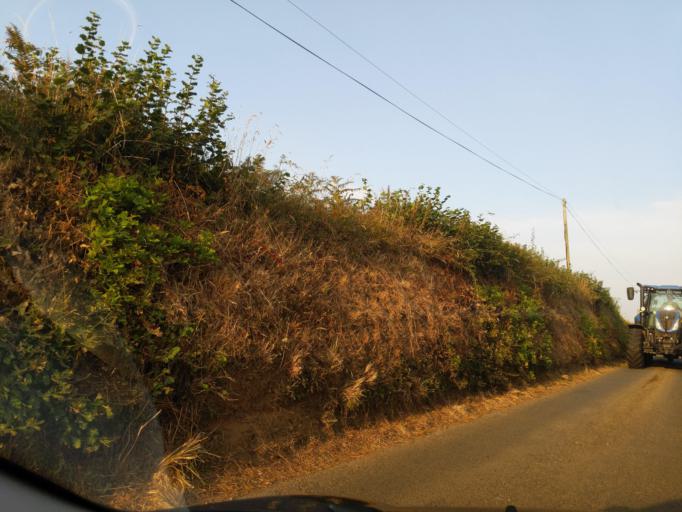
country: GB
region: England
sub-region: Cornwall
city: Fowey
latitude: 50.3676
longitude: -4.5882
